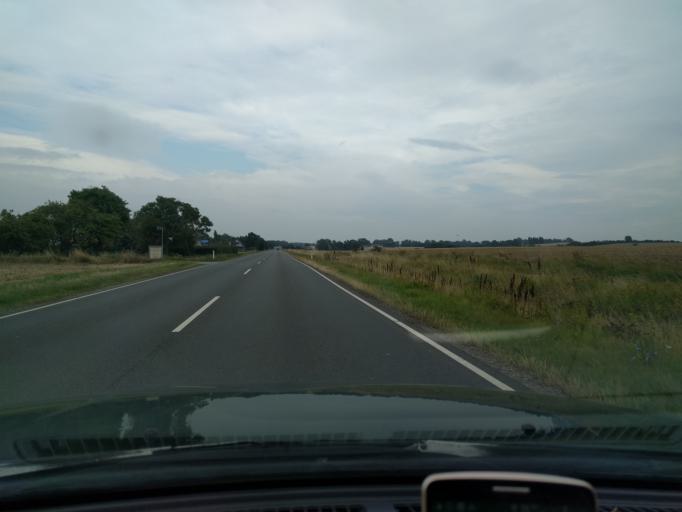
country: DK
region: Zealand
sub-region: Slagelse Kommune
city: Korsor
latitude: 55.3206
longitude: 11.2051
